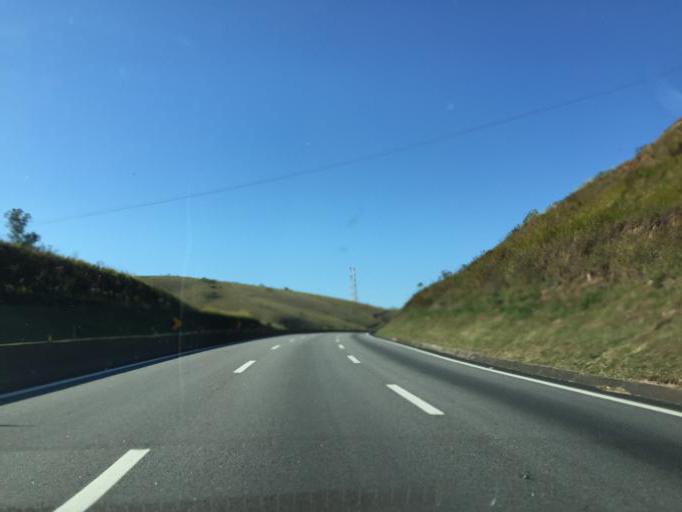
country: BR
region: Sao Paulo
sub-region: Cruzeiro
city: Cruzeiro
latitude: -22.6420
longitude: -44.9471
